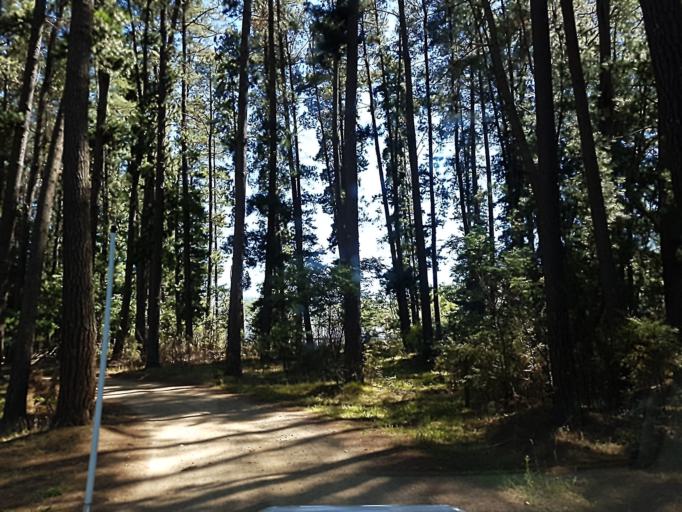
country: AU
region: Victoria
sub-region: Alpine
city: Mount Beauty
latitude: -36.8948
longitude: 147.0686
